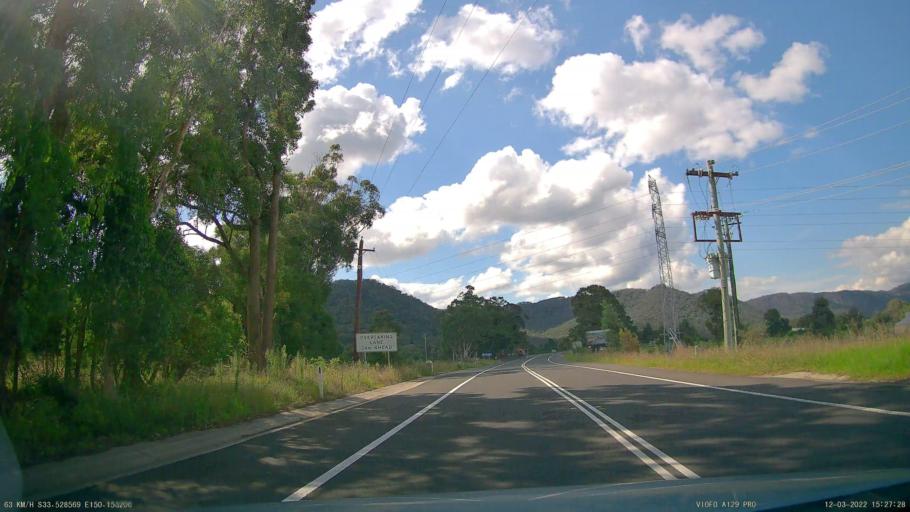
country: AU
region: New South Wales
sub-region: Lithgow
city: Bowenfels
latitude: -33.5283
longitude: 150.1532
